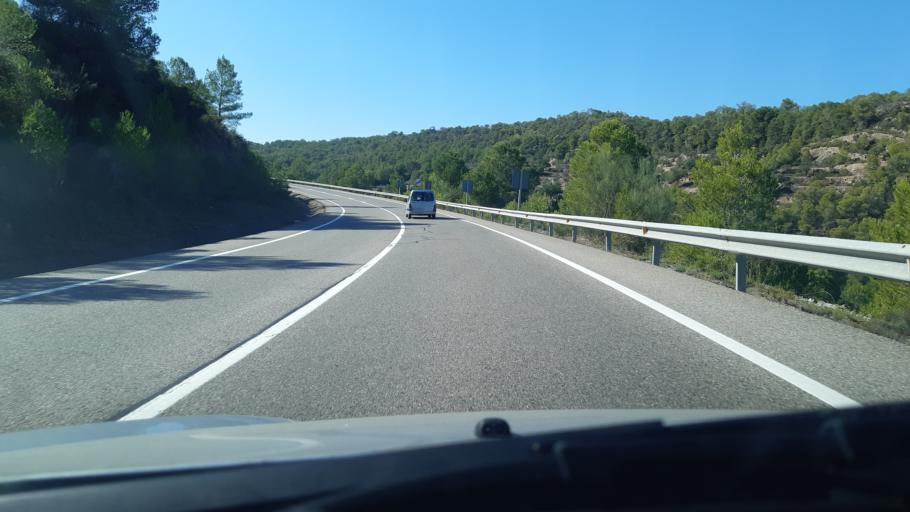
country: ES
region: Catalonia
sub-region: Provincia de Tarragona
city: Rasquera
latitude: 41.0075
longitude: 0.5991
